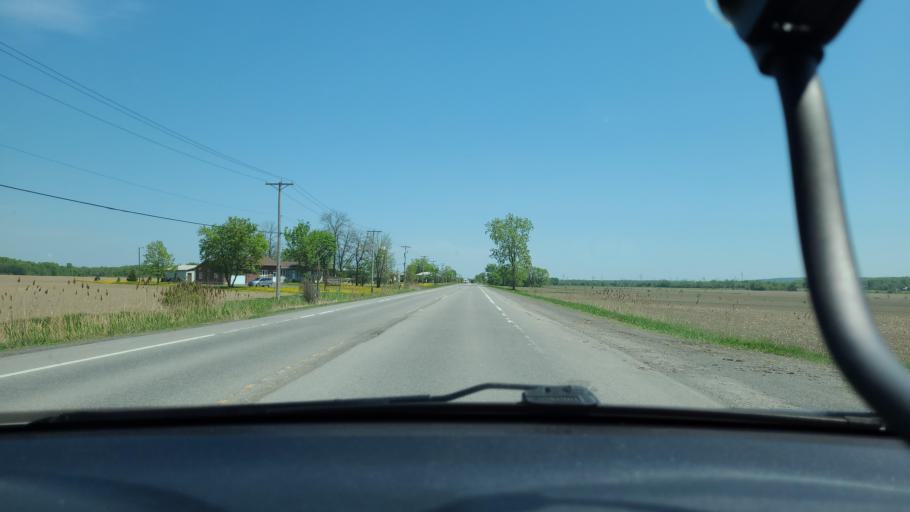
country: CA
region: Quebec
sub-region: Laurentides
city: Mirabel
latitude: 45.6161
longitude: -74.0913
